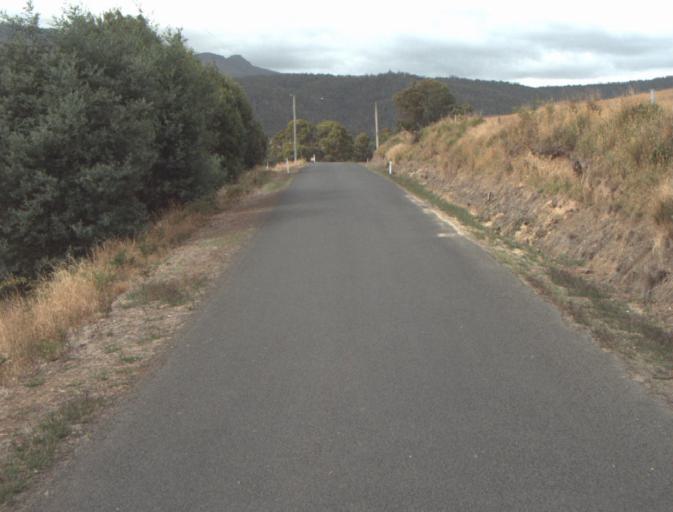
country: AU
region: Tasmania
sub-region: Dorset
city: Scottsdale
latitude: -41.4614
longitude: 147.5954
